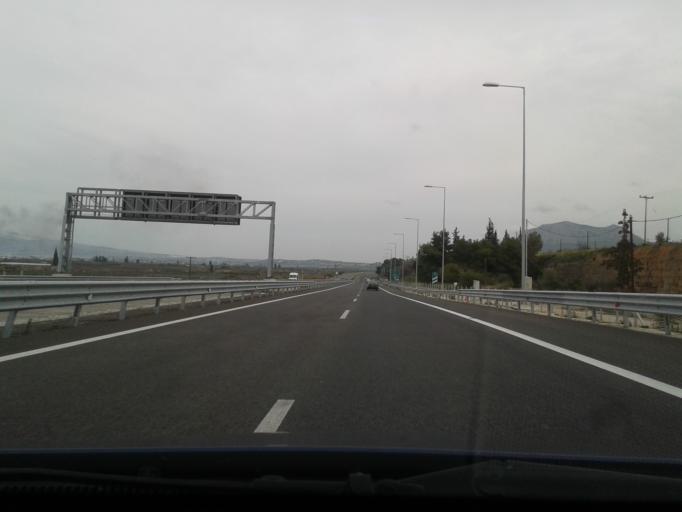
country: GR
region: Peloponnese
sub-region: Nomos Korinthias
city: Zevgolateio
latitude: 37.9223
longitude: 22.8088
